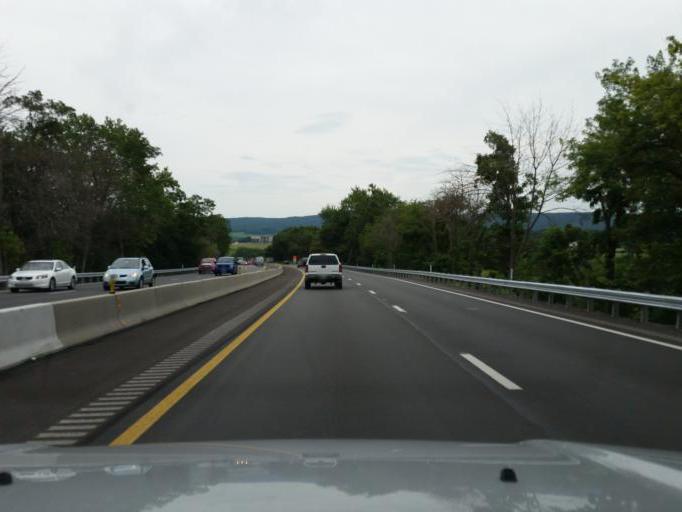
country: US
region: Pennsylvania
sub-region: Westmoreland County
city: Lawson Heights
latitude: 40.2824
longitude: -79.4142
